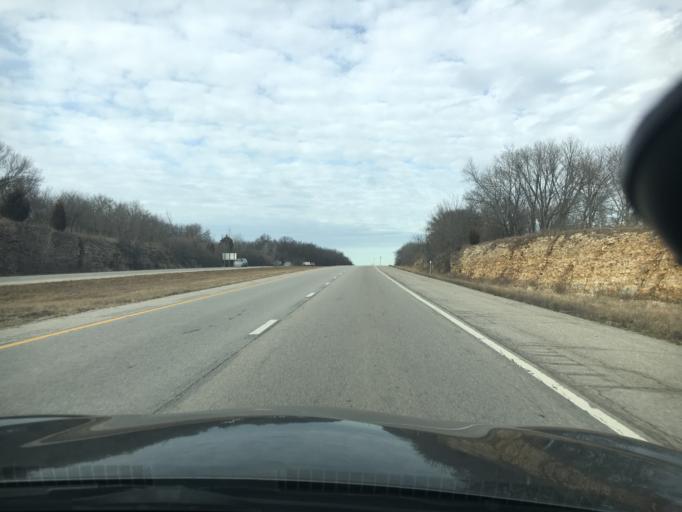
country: US
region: Missouri
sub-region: Cass County
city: Belton
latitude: 38.8151
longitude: -94.6758
